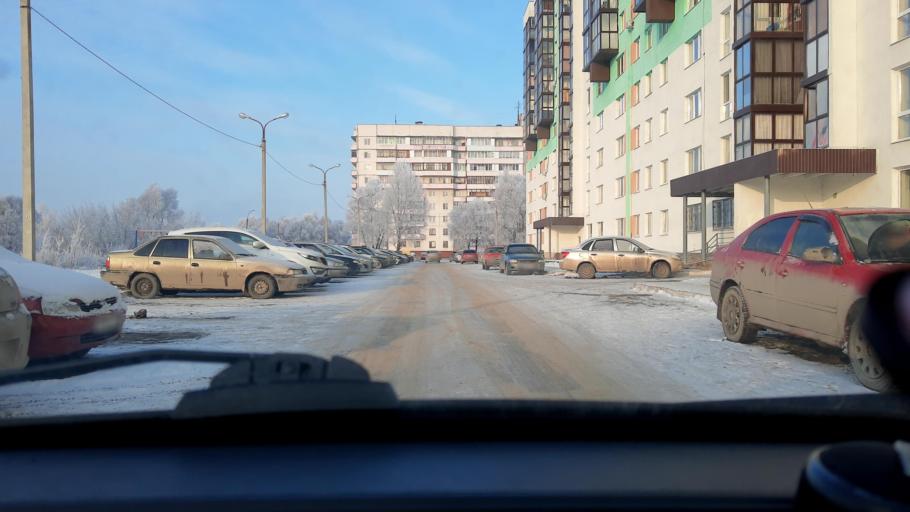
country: RU
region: Bashkortostan
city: Iglino
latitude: 54.7559
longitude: 56.2341
